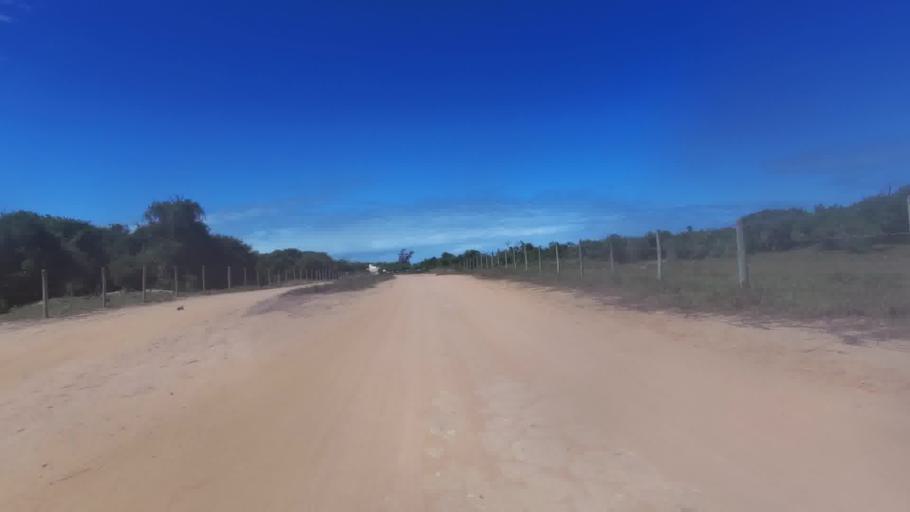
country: BR
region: Espirito Santo
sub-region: Marataizes
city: Marataizes
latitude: -21.1978
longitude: -40.9393
